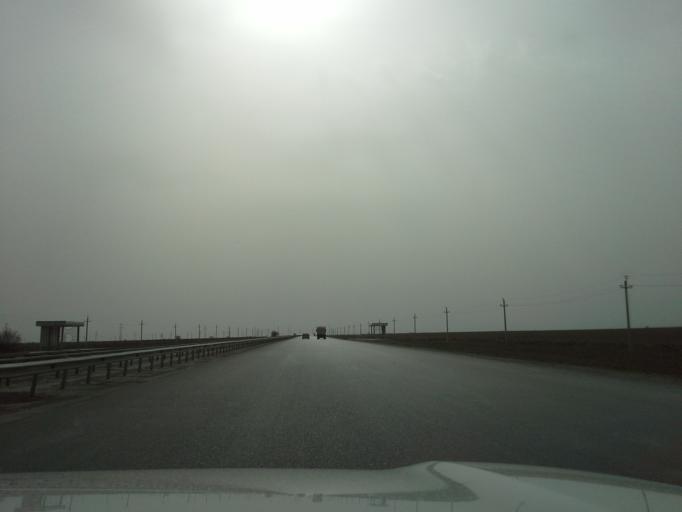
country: IR
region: Razavi Khorasan
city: Dargaz
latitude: 37.5566
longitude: 59.3678
